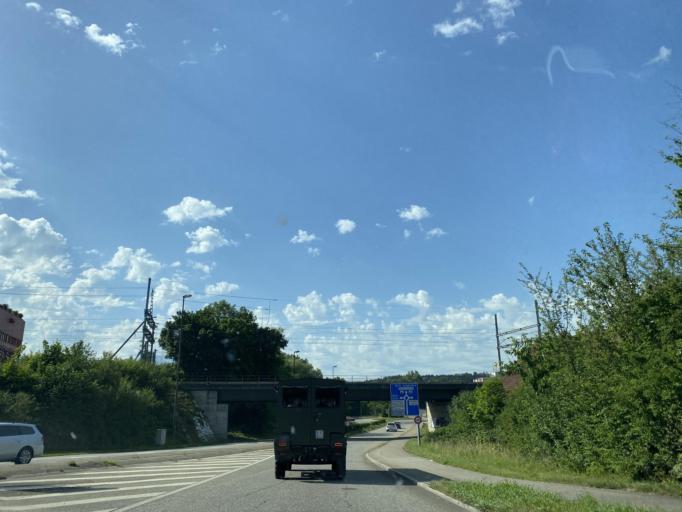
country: CH
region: Aargau
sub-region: Bezirk Zofingen
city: Rothrist
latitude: 47.3111
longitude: 7.8939
